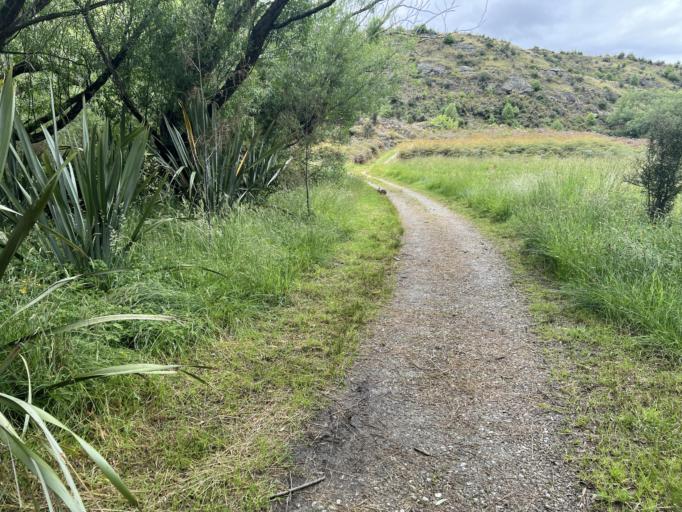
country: NZ
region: Otago
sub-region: Queenstown-Lakes District
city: Wanaka
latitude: -44.6484
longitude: 168.9623
